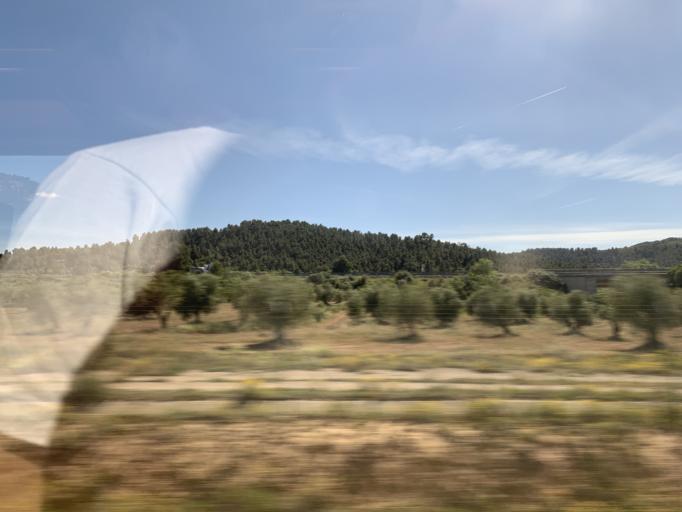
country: ES
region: Catalonia
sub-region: Provincia de Lleida
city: Vinaixa
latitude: 41.4403
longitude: 0.9231
